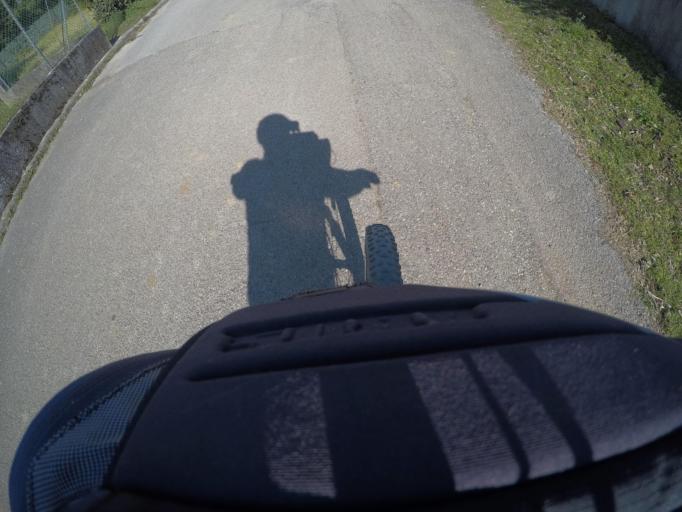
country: IT
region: Friuli Venezia Giulia
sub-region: Provincia di Udine
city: Lestizza
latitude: 45.9683
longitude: 13.1558
